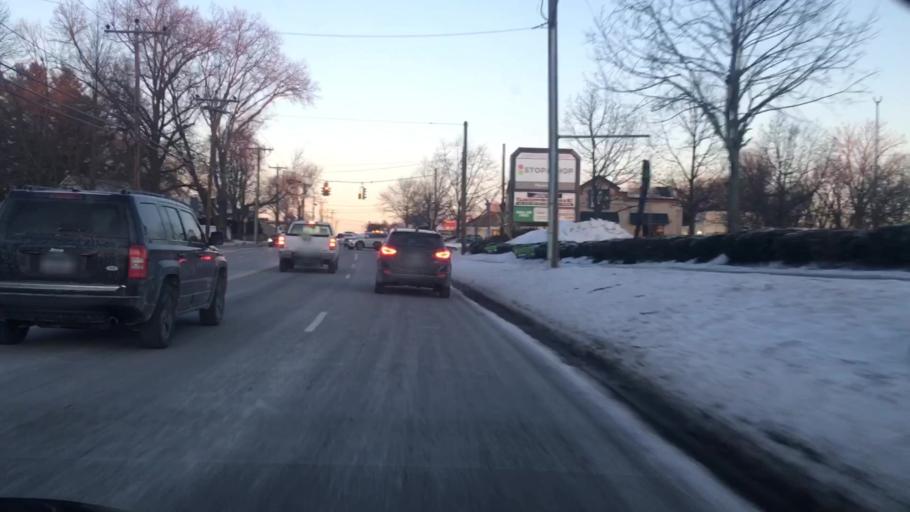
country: US
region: Connecticut
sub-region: Hartford County
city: Manchester
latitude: 41.7806
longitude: -72.5412
